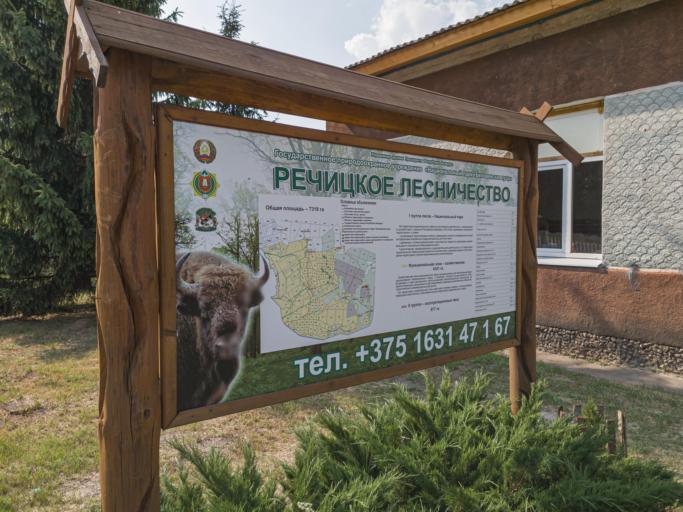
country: BY
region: Brest
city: Kamyanyets
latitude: 52.3938
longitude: 24.0025
